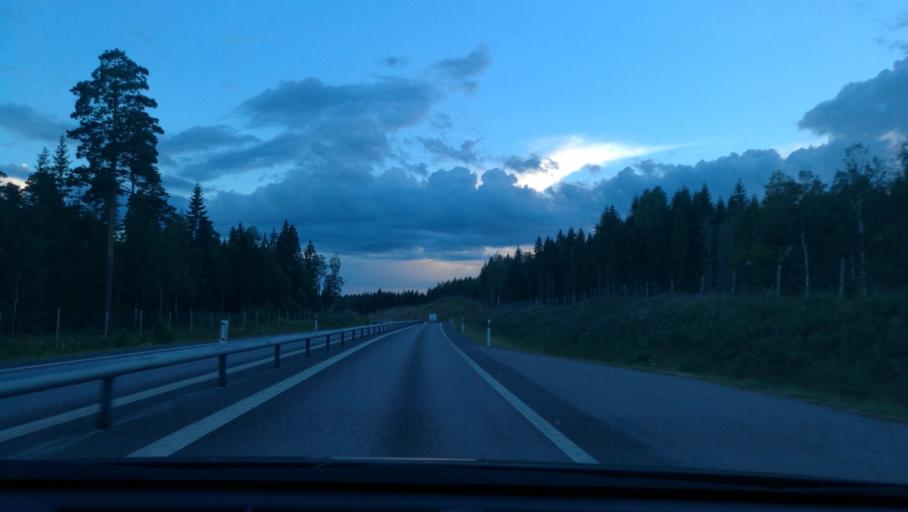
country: SE
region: Soedermanland
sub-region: Katrineholms Kommun
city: Katrineholm
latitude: 58.9390
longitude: 16.2059
